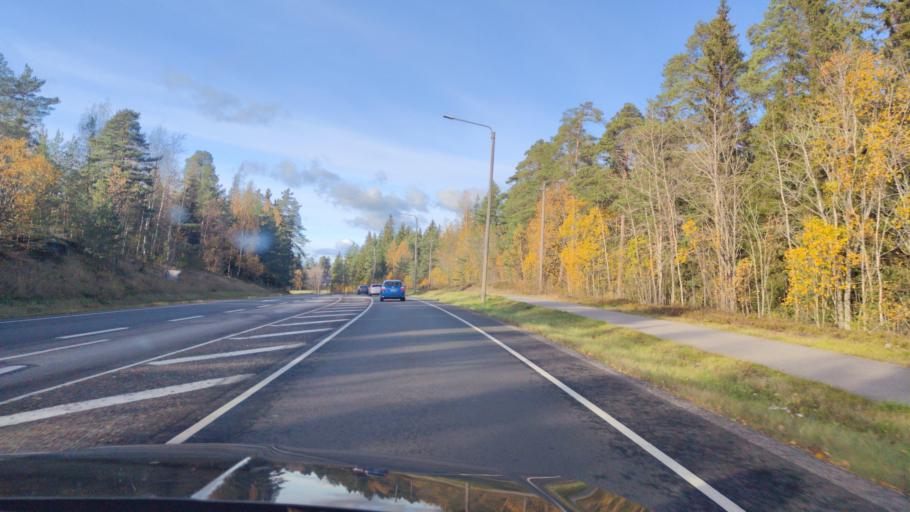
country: FI
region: Varsinais-Suomi
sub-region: Turku
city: Kaarina
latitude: 60.4585
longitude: 22.3653
